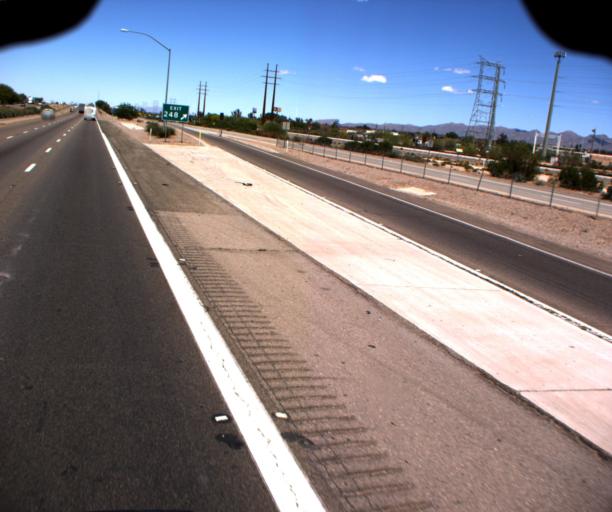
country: US
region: Arizona
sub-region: Pima County
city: Flowing Wells
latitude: 32.3334
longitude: -111.0617
